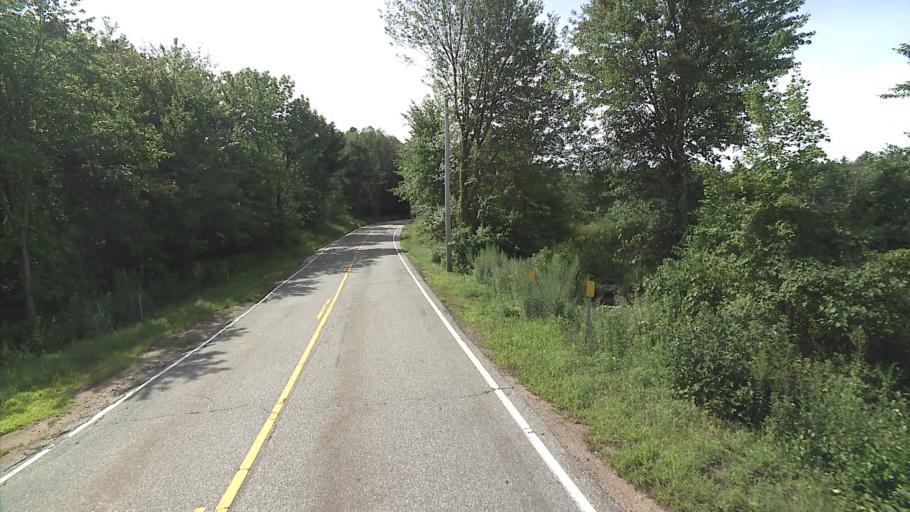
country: US
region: Massachusetts
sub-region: Hampden County
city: Holland
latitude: 41.9718
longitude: -72.1125
